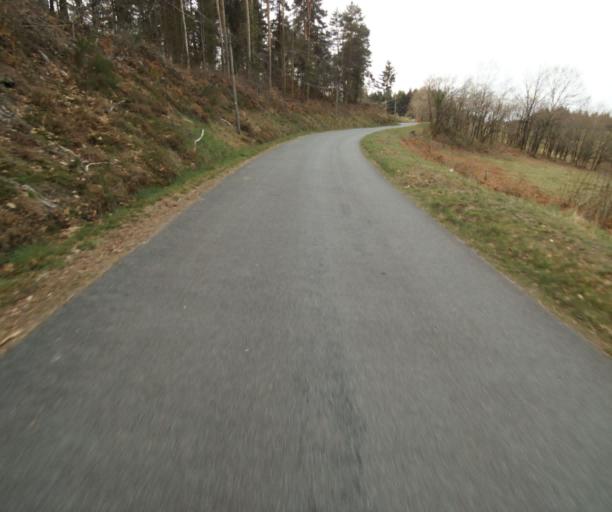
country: FR
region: Limousin
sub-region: Departement de la Correze
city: Treignac
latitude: 45.4672
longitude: 1.8191
